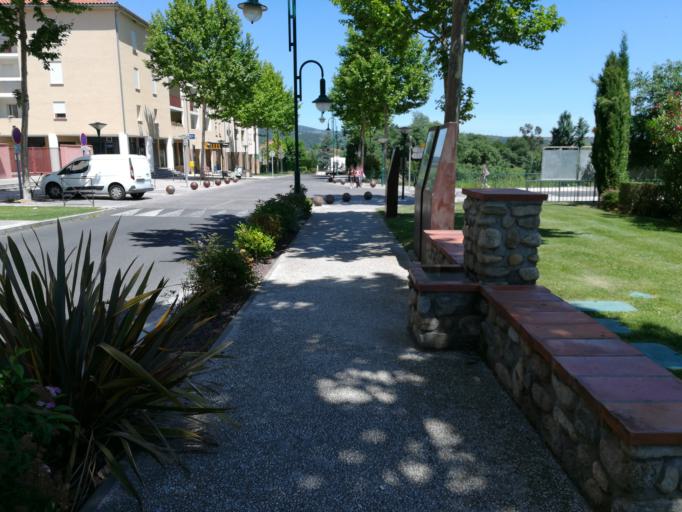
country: FR
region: Languedoc-Roussillon
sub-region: Departement des Pyrenees-Orientales
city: Ceret
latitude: 42.4848
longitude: 2.7452
